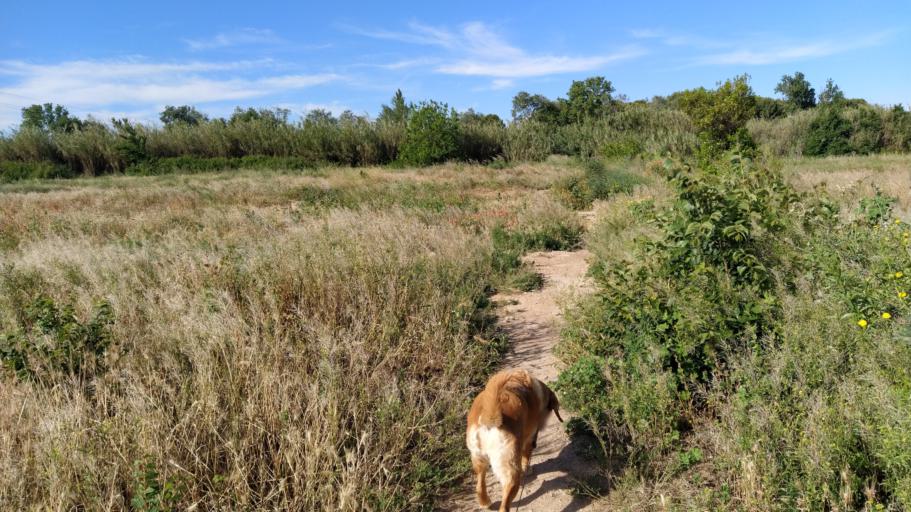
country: ES
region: Aragon
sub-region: Provincia de Zaragoza
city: Oliver-Valdefierro, Oliver, Valdefierro
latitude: 41.6400
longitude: -0.9389
